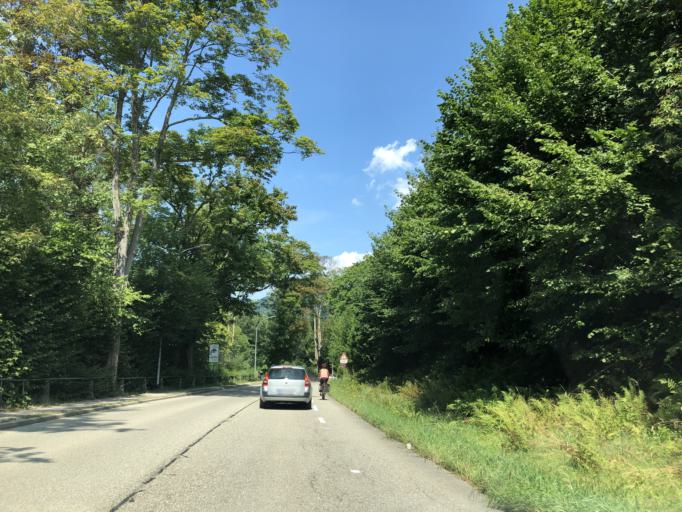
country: DE
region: Baden-Wuerttemberg
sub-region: Karlsruhe Region
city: Baden-Baden
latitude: 48.7356
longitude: 8.2542
